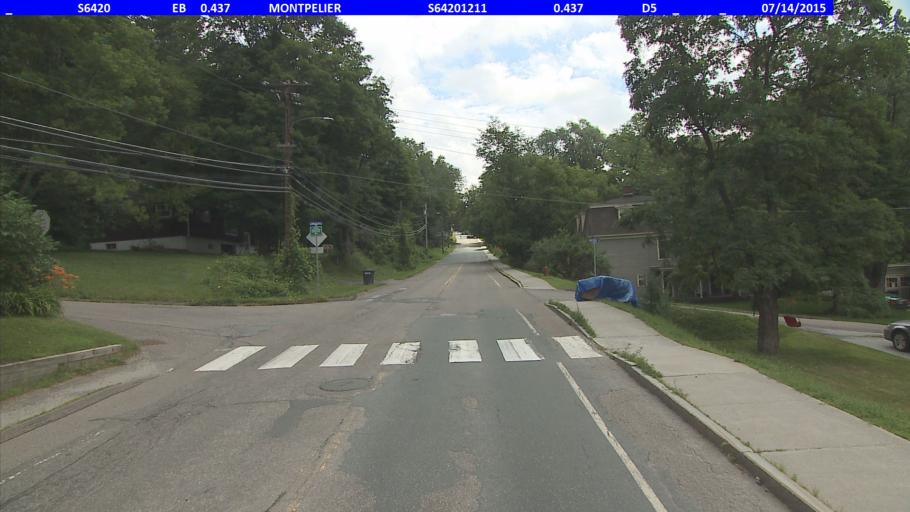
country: US
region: Vermont
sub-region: Washington County
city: Montpelier
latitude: 44.2616
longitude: -72.5645
